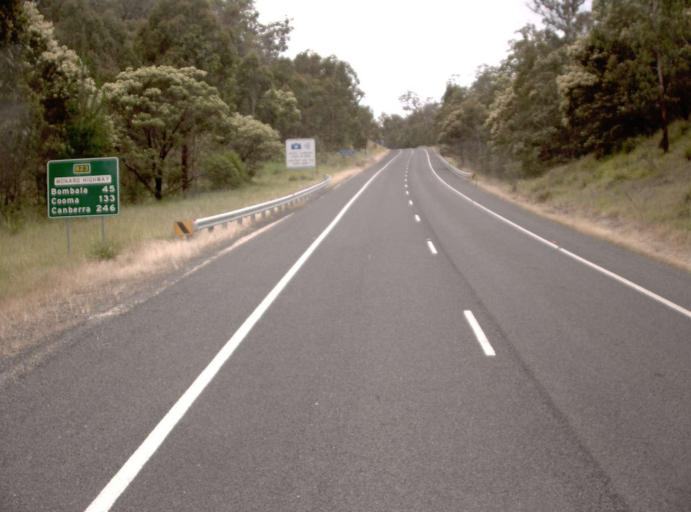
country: AU
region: New South Wales
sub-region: Bombala
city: Bombala
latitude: -37.2303
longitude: 149.2756
